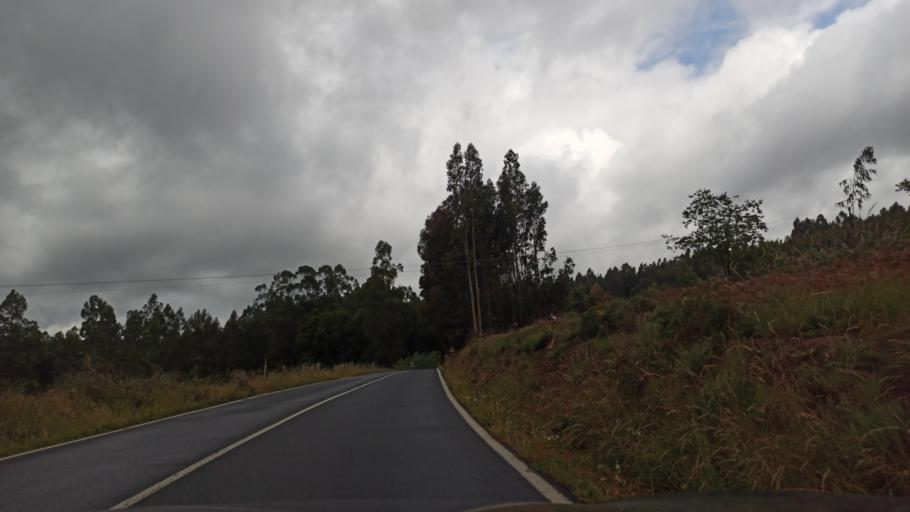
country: ES
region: Galicia
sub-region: Provincia da Coruna
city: Santiso
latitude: 42.7831
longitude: -8.0492
